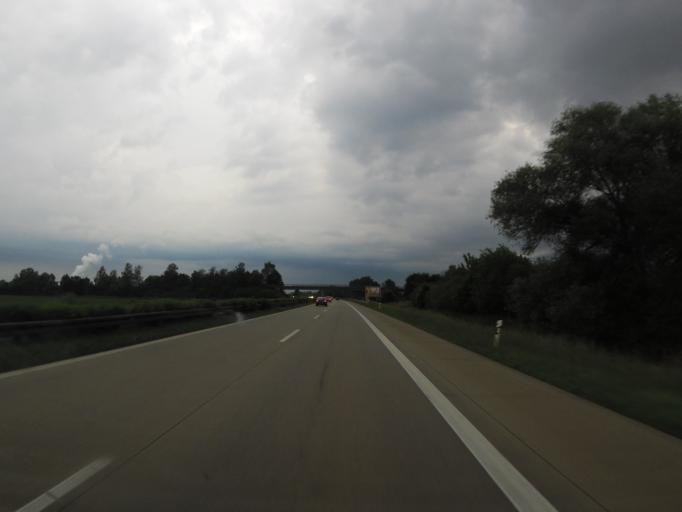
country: DE
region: Bavaria
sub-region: Lower Bavaria
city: Worth an der Isar
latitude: 48.6351
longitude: 12.3558
